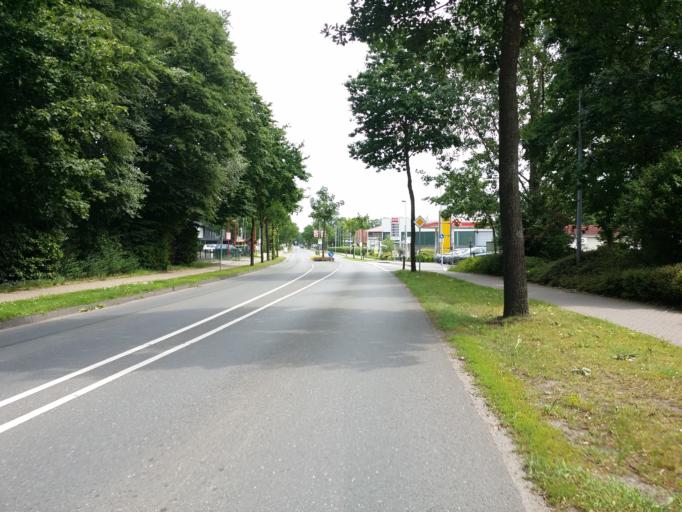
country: DE
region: Lower Saxony
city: Wiefelstede
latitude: 53.2512
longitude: 8.1193
